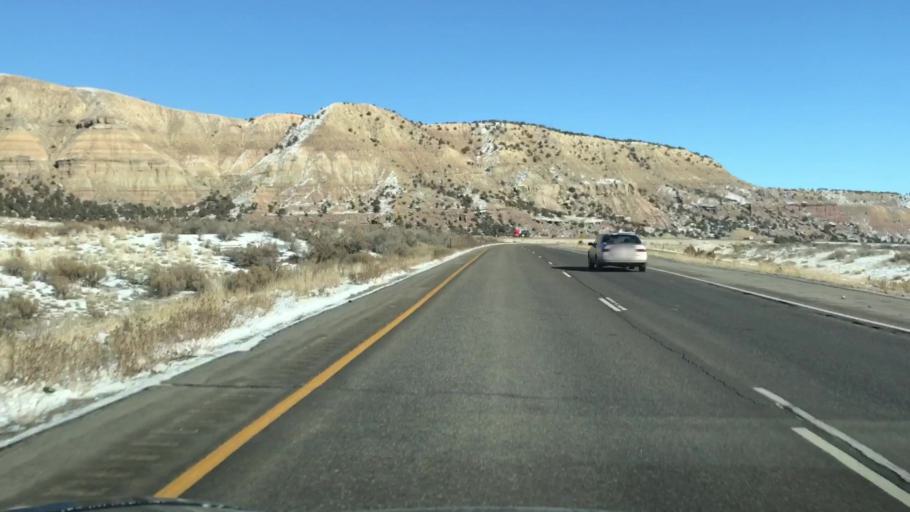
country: US
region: Colorado
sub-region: Garfield County
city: Battlement Mesa
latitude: 39.4999
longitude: -107.9370
